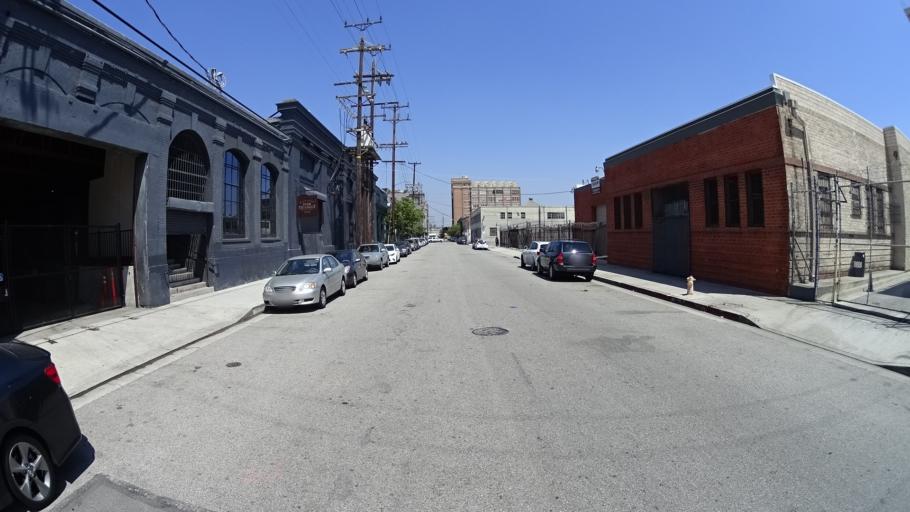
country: US
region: California
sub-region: Los Angeles County
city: Los Angeles
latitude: 34.0360
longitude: -118.2360
